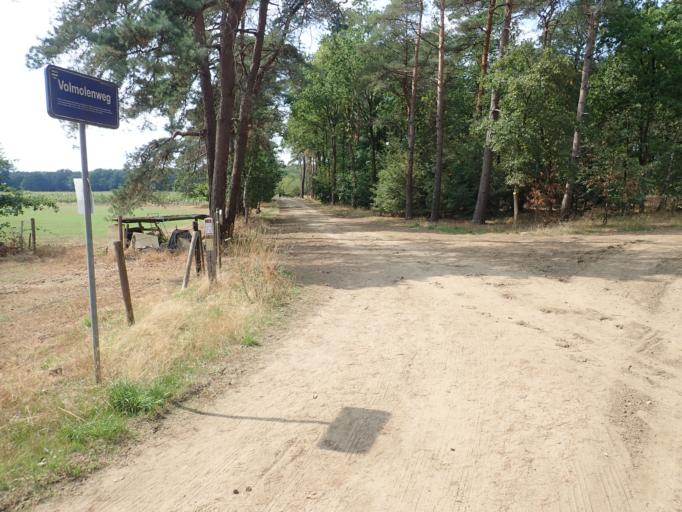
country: BE
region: Flanders
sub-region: Provincie Antwerpen
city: Meerhout
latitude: 51.1558
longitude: 5.0868
